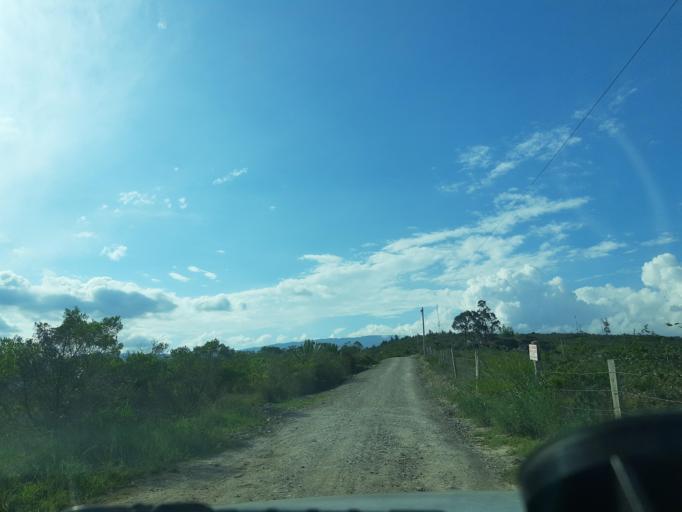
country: CO
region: Boyaca
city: Villa de Leiva
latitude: 5.6610
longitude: -73.5510
